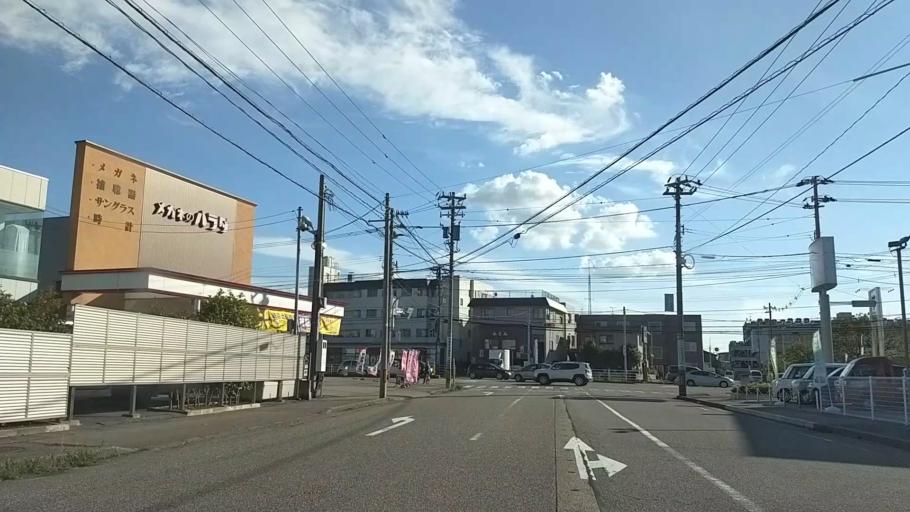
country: JP
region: Ishikawa
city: Kanazawa-shi
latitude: 36.5807
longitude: 136.6349
